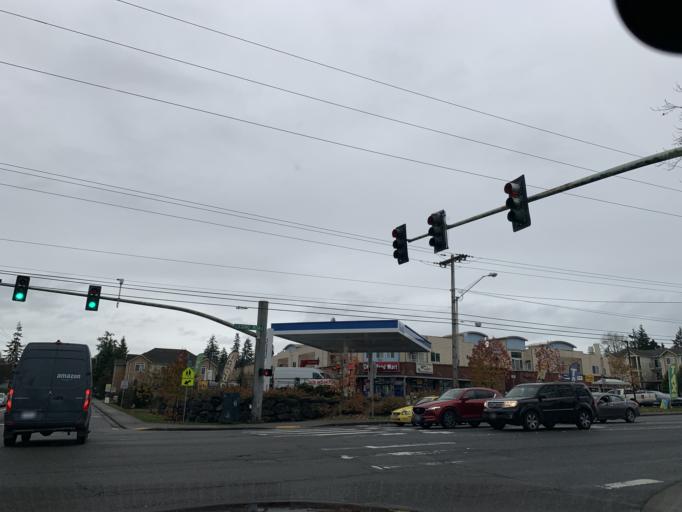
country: US
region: Washington
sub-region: Snohomish County
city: Mukilteo
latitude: 47.9220
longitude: -122.2406
